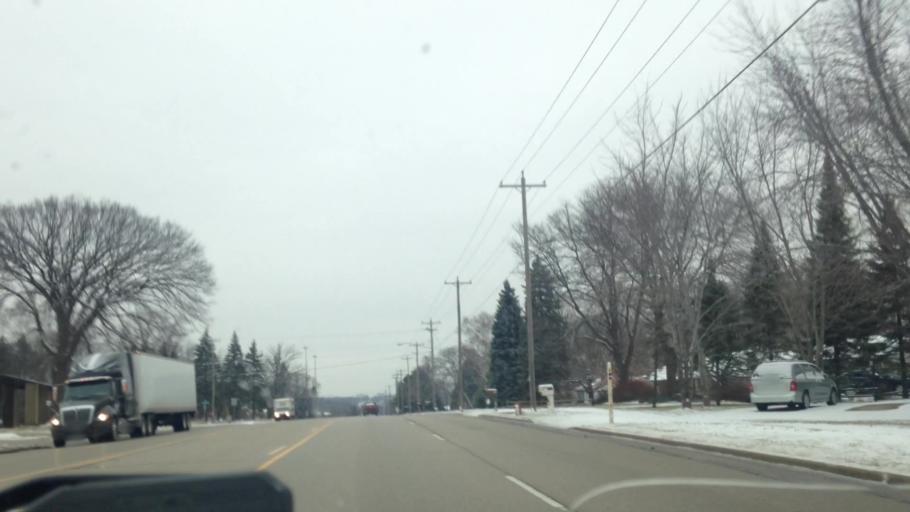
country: US
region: Wisconsin
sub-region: Waukesha County
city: Menomonee Falls
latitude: 43.1645
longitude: -88.1039
